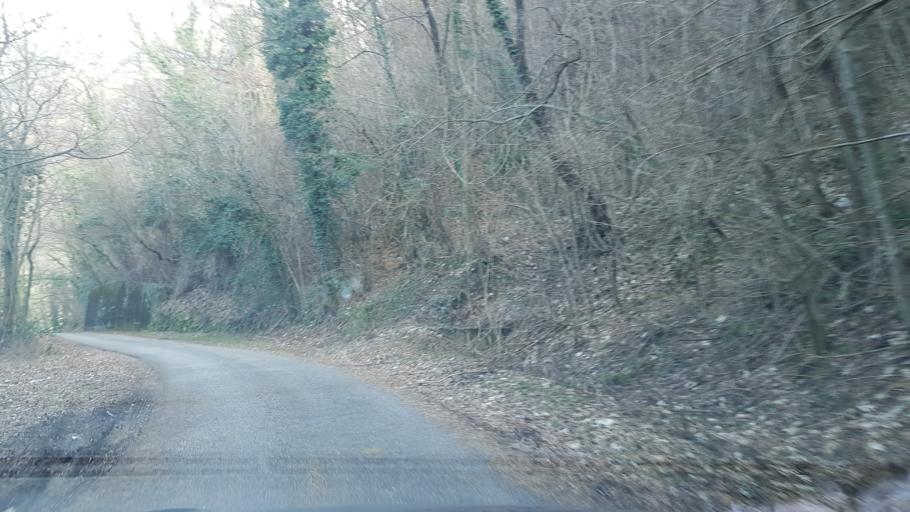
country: IT
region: Friuli Venezia Giulia
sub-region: Provincia di Udine
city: Montenars
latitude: 46.2830
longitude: 13.1566
